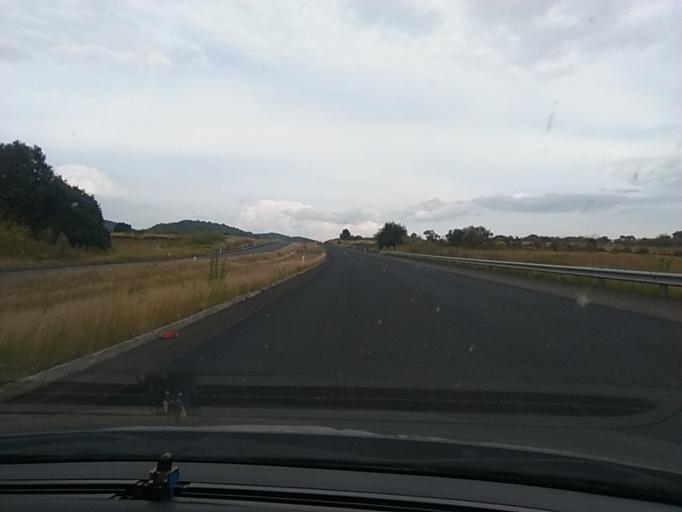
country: MX
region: Mexico
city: Huaniqueo de Morales
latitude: 19.8831
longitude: -101.4423
